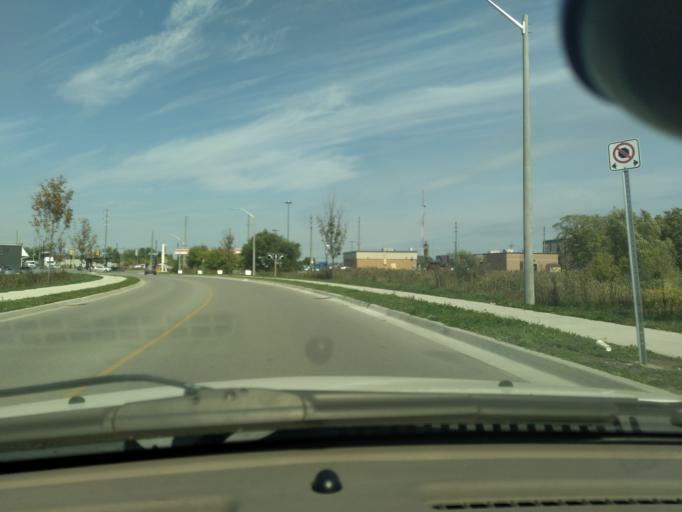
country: CA
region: Ontario
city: Bradford West Gwillimbury
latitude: 44.1143
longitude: -79.5574
